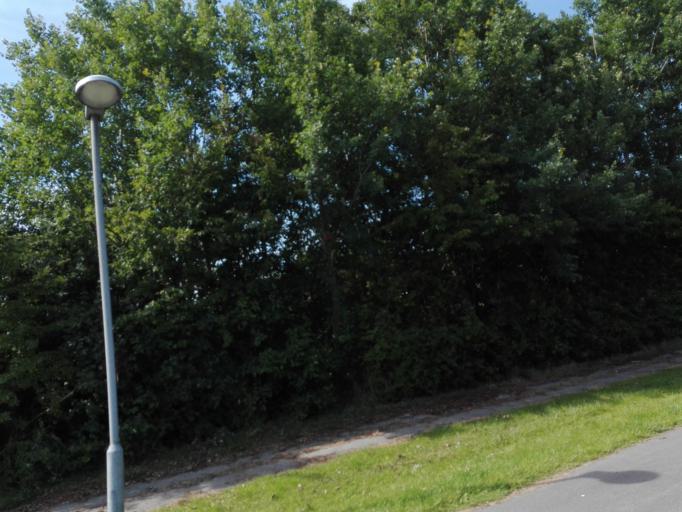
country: DK
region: Central Jutland
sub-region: Arhus Kommune
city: Marslet
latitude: 56.0866
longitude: 10.1499
